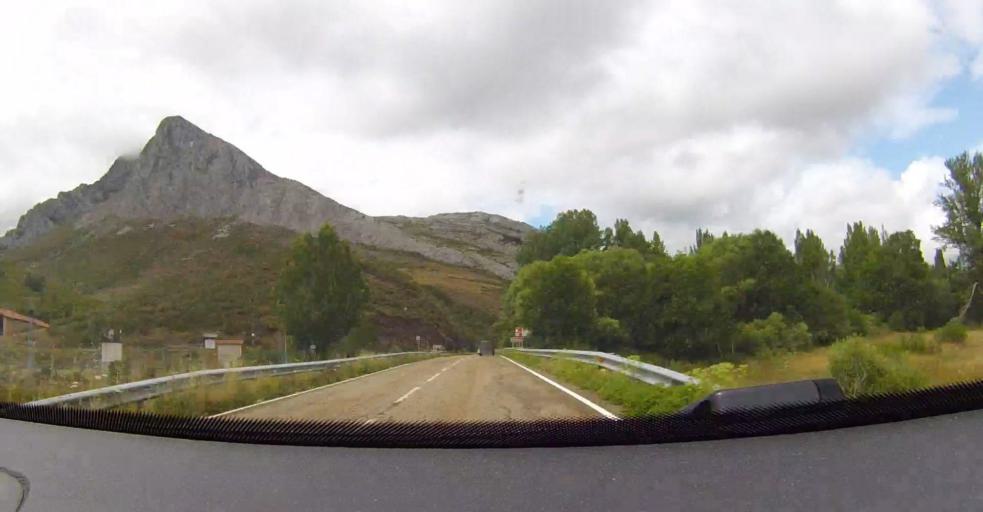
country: ES
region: Castille and Leon
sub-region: Provincia de Leon
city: Puebla de Lillo
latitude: 42.9887
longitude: -5.2590
